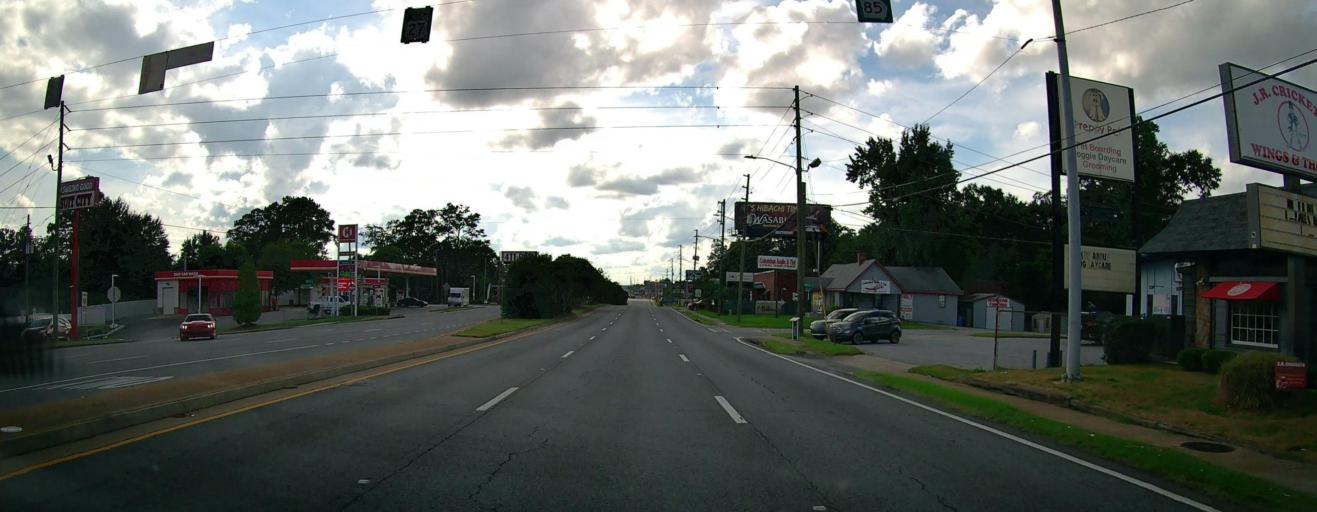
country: US
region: Georgia
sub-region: Muscogee County
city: Columbus
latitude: 32.5069
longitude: -84.9549
